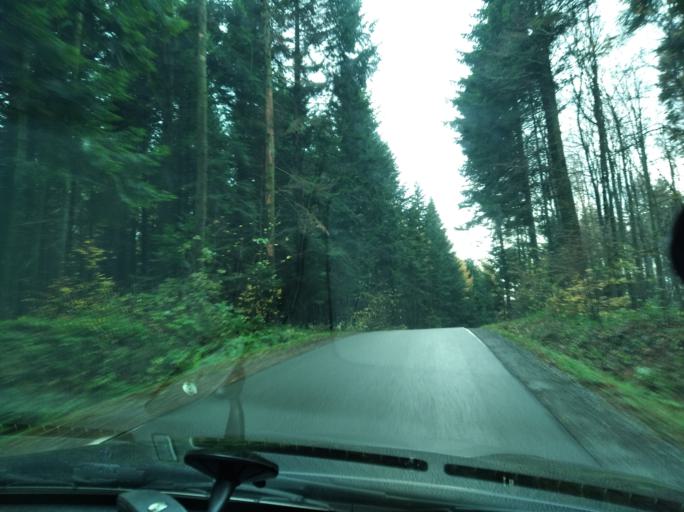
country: PL
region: Subcarpathian Voivodeship
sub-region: Powiat strzyzowski
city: Strzyzow
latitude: 49.9040
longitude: 21.7846
